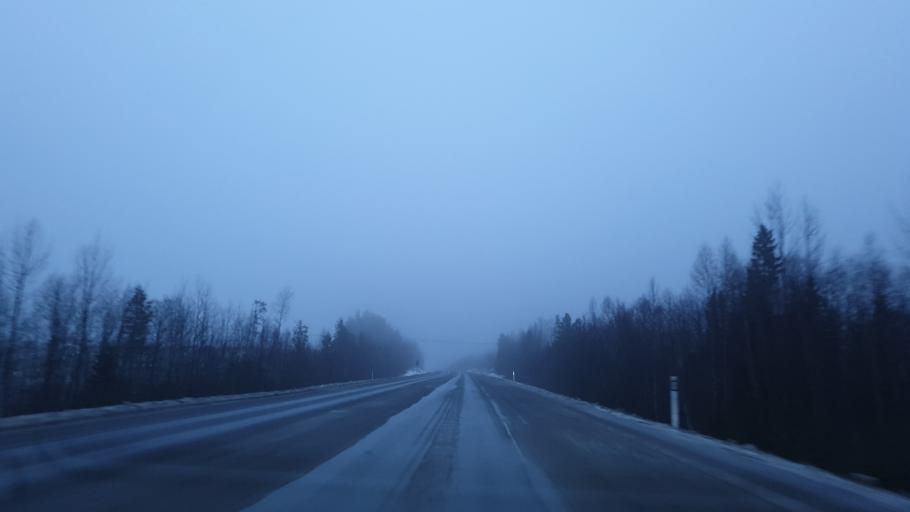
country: SE
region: Vaesterbotten
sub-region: Umea Kommun
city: Holmsund
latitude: 63.7687
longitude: 20.3368
